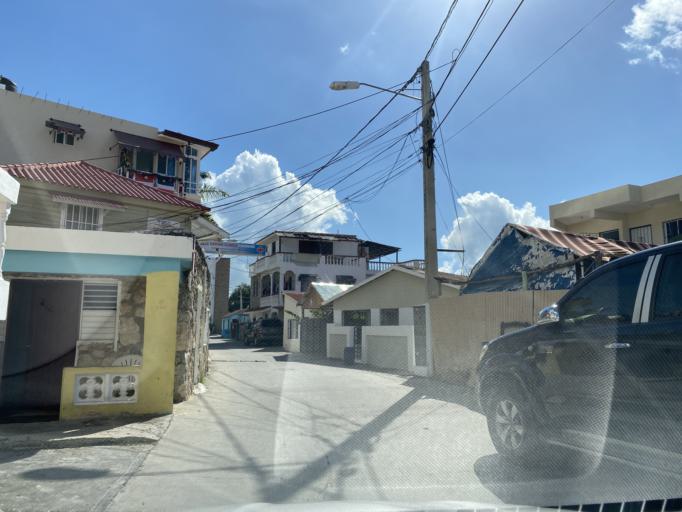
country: DO
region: La Romana
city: La Romana
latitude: 18.3684
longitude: -68.8386
